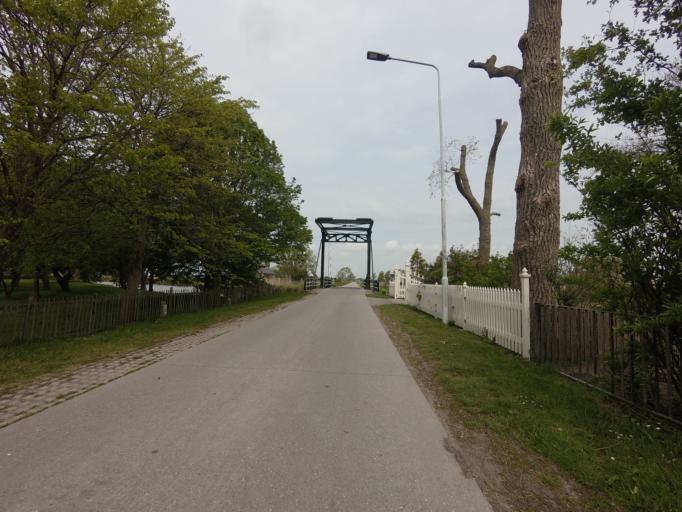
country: NL
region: Friesland
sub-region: Sudwest Fryslan
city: Makkum
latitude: 53.0630
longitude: 5.4615
